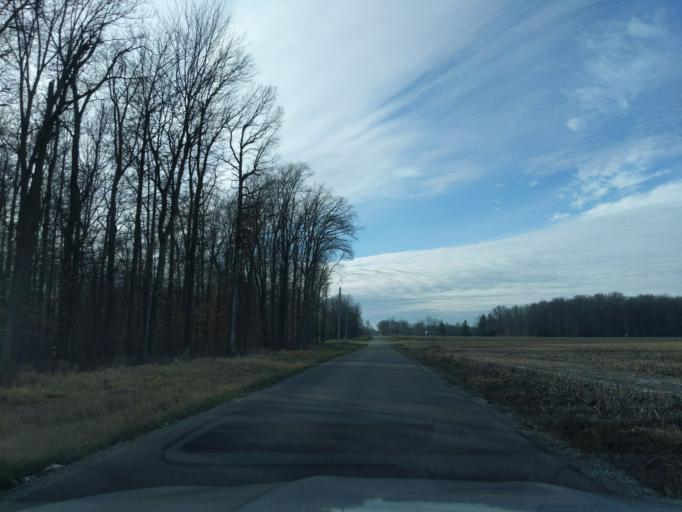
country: US
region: Indiana
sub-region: Decatur County
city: Westport
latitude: 39.1902
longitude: -85.4961
